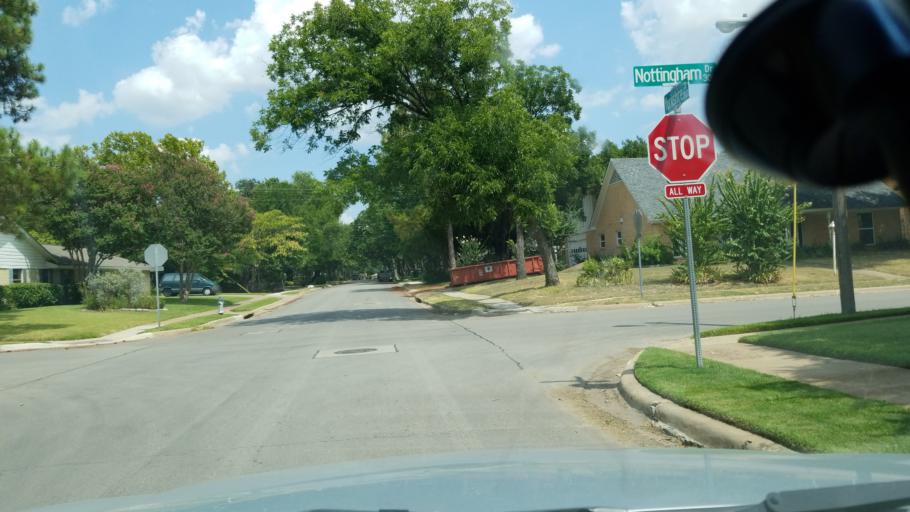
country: US
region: Texas
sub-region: Dallas County
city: Irving
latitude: 32.8185
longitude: -96.9829
